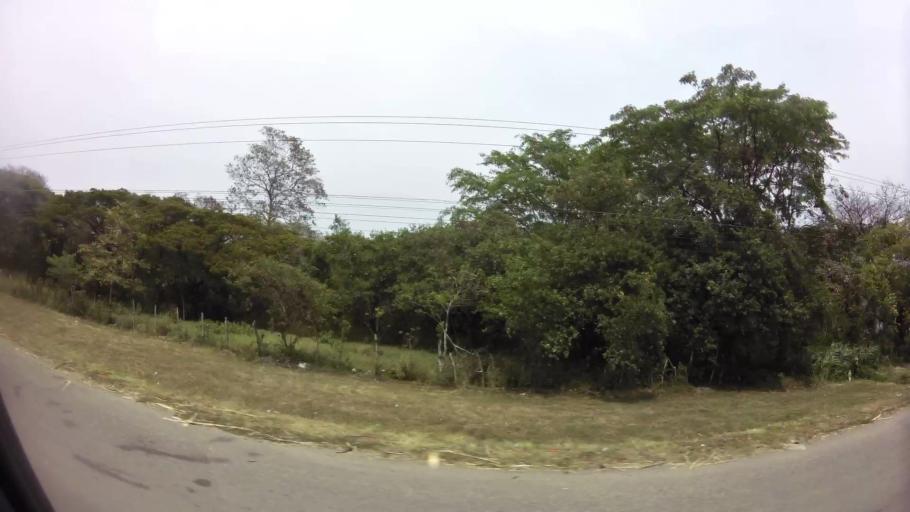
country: HN
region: Cortes
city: Nuevo Chamelecon
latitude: 15.3680
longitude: -87.9854
